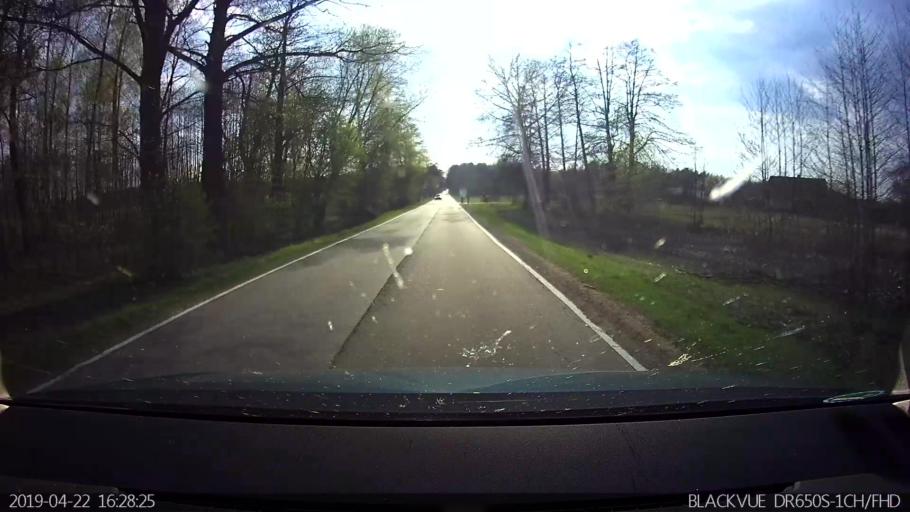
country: PL
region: Podlasie
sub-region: Powiat siemiatycki
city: Milejczyce
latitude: 52.5401
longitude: 23.1821
